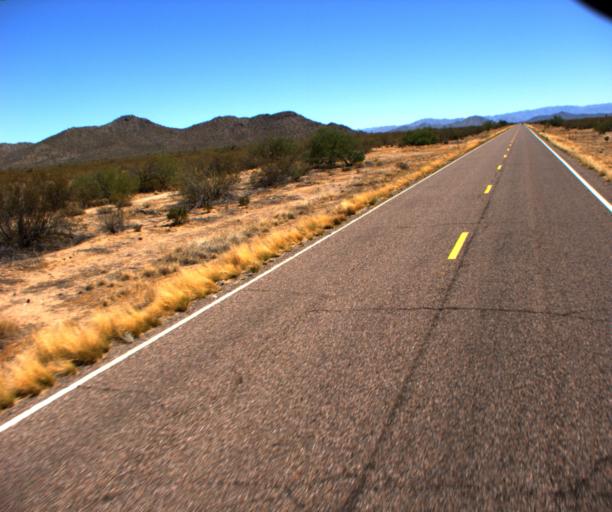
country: US
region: Arizona
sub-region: Yavapai County
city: Congress
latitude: 34.0172
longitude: -113.1001
